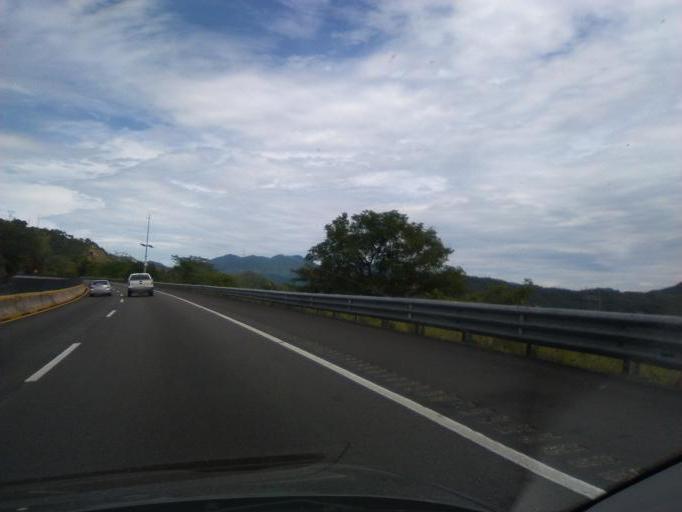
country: MX
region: Guerrero
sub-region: Chilpancingo de los Bravo
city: Cajelitos
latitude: 17.3038
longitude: -99.4971
